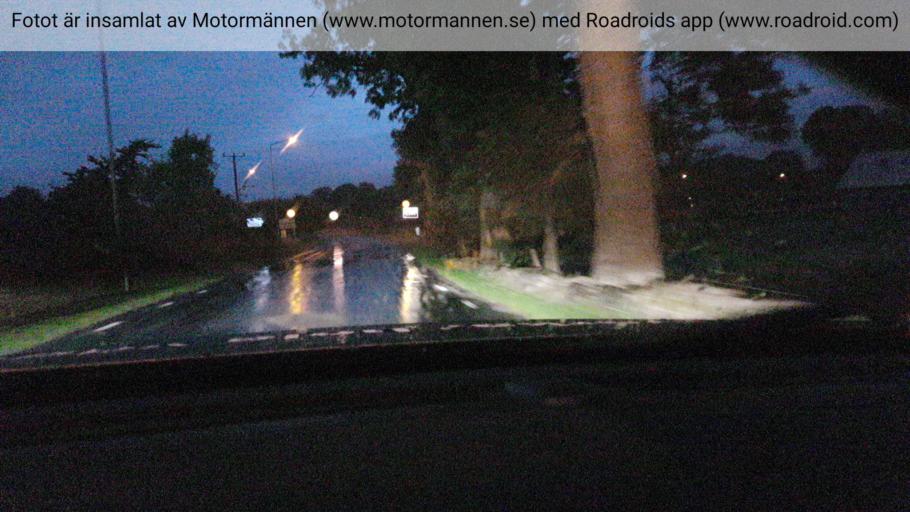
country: SE
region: Vaestra Goetaland
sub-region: Skovde Kommun
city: Skultorp
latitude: 58.2546
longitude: 13.7856
